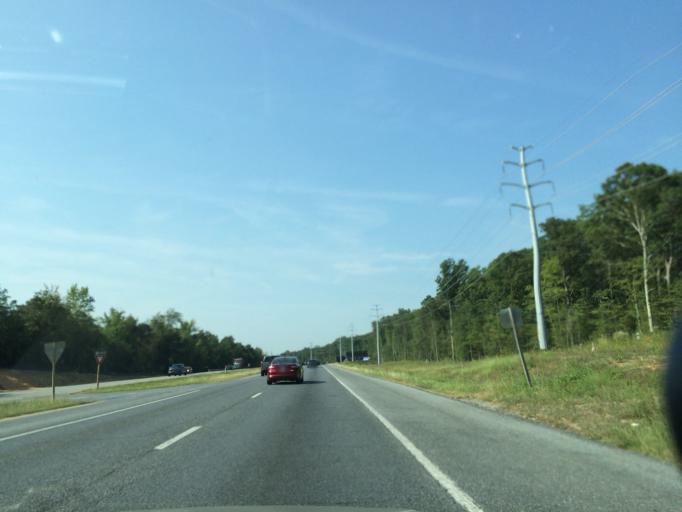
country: US
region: Maryland
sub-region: Charles County
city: Saint Charles
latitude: 38.6049
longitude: -76.9327
